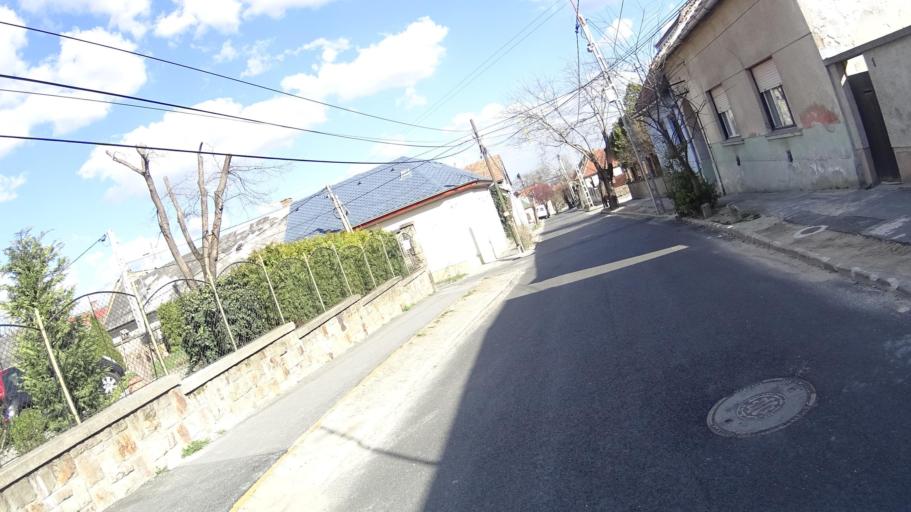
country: HU
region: Budapest
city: Budapest XXII. keruelet
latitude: 47.4258
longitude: 19.0309
